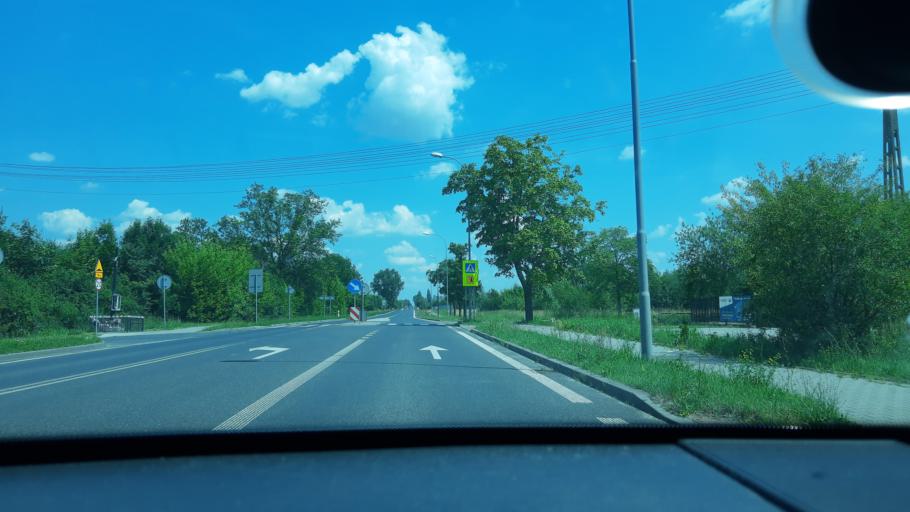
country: PL
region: Lodz Voivodeship
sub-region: Powiat zdunskowolski
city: Zapolice
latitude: 51.6054
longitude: 18.8491
